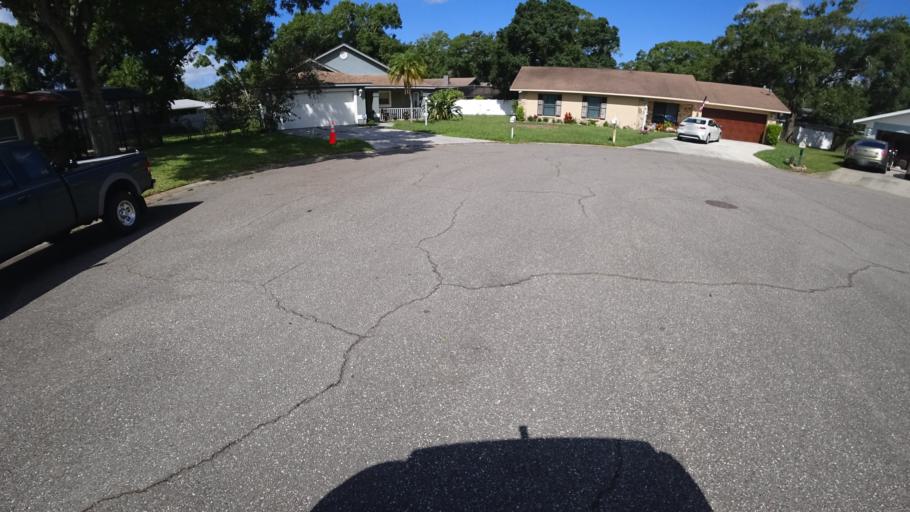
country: US
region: Florida
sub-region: Sarasota County
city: Desoto Lakes
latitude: 27.3905
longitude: -82.4995
